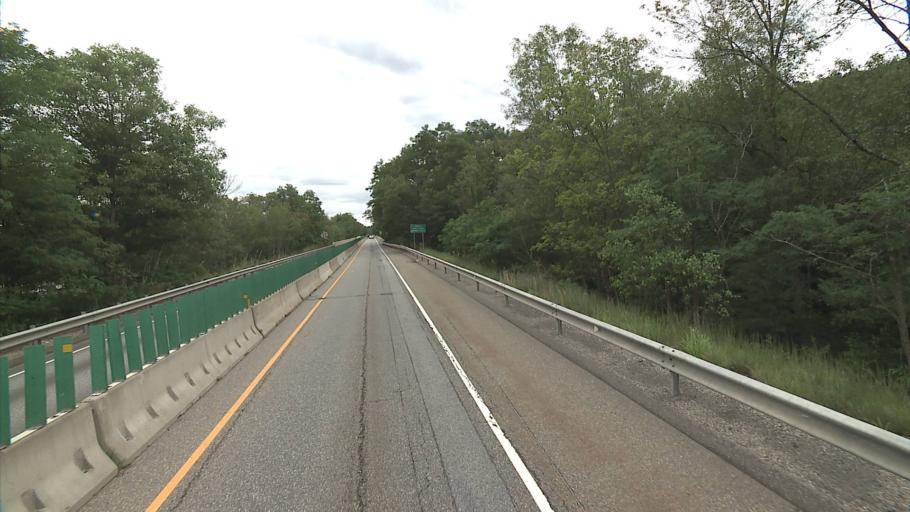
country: US
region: Connecticut
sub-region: Litchfield County
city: Northwest Harwinton
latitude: 41.7404
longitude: -73.1120
